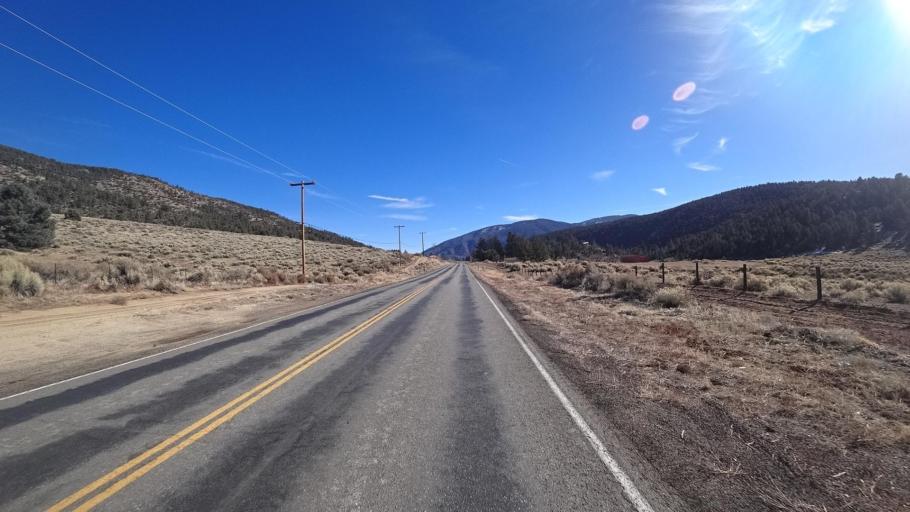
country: US
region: California
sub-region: Kern County
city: Frazier Park
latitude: 34.8321
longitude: -119.0289
